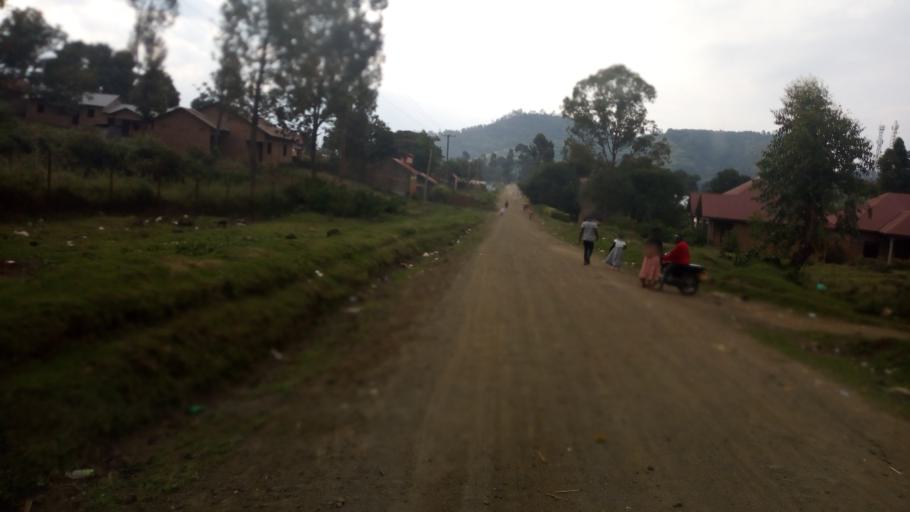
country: UG
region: Western Region
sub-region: Kisoro District
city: Kisoro
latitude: -1.2897
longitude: 29.6920
